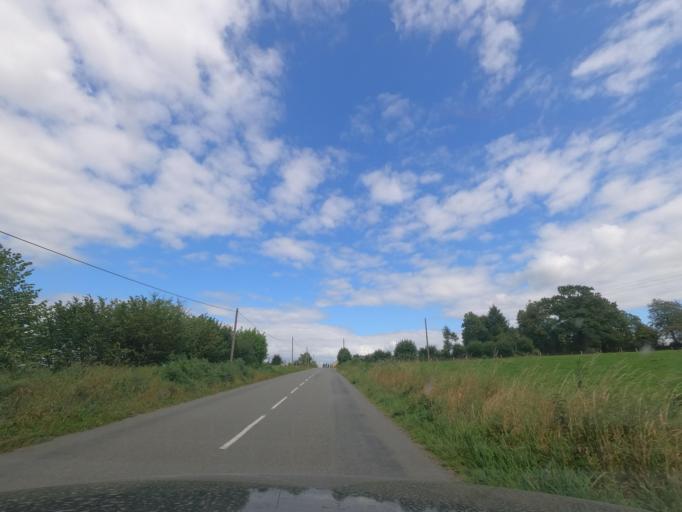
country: FR
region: Pays de la Loire
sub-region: Departement de la Mayenne
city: Landivy
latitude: 48.4590
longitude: -1.0573
